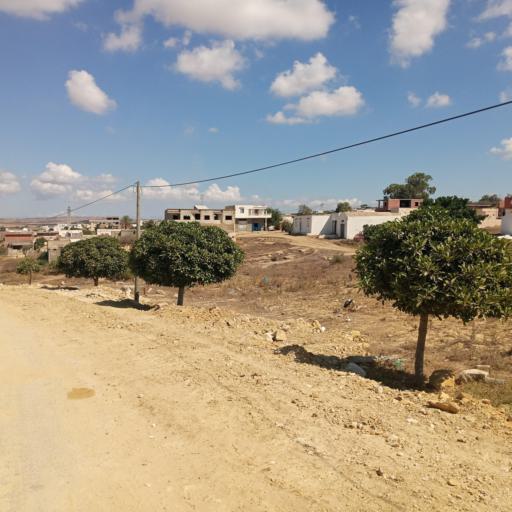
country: TN
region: Nabul
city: Qulaybiyah
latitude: 36.8569
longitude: 11.0348
